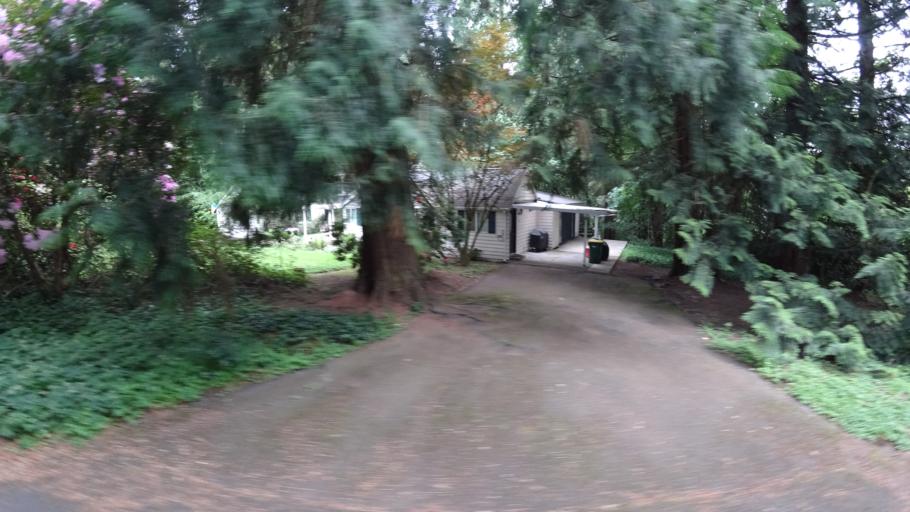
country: US
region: Oregon
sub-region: Washington County
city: Garden Home-Whitford
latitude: 45.4693
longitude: -122.7438
